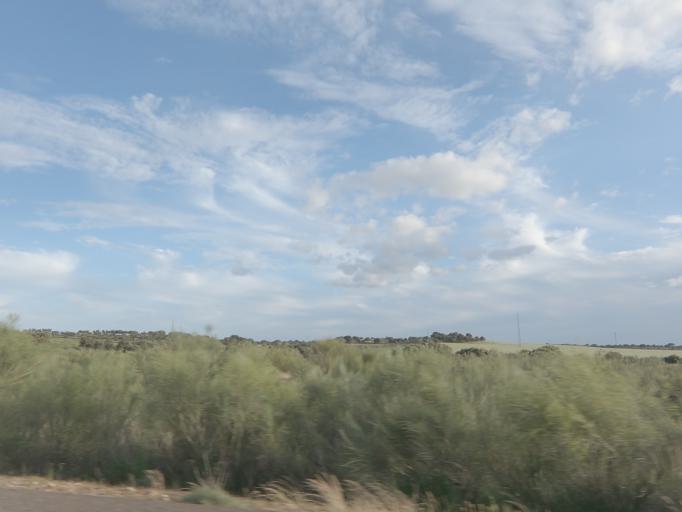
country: ES
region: Extremadura
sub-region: Provincia de Badajoz
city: Talavera La Real
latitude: 38.8681
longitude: -6.8278
